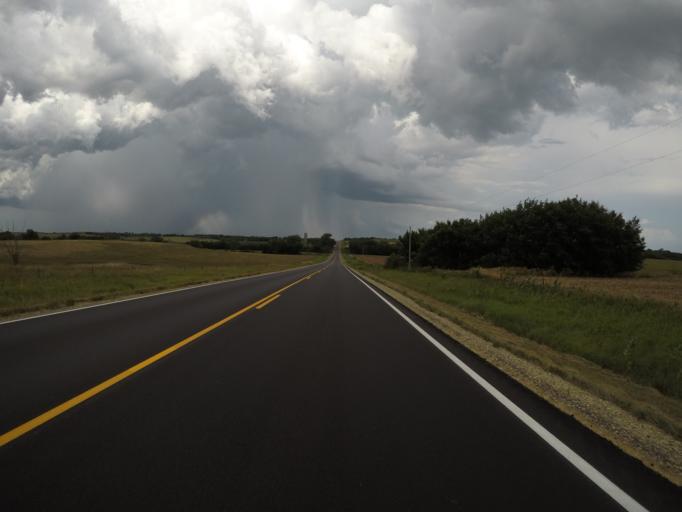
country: US
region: Kansas
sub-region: Clay County
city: Clay Center
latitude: 39.4368
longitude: -96.8339
